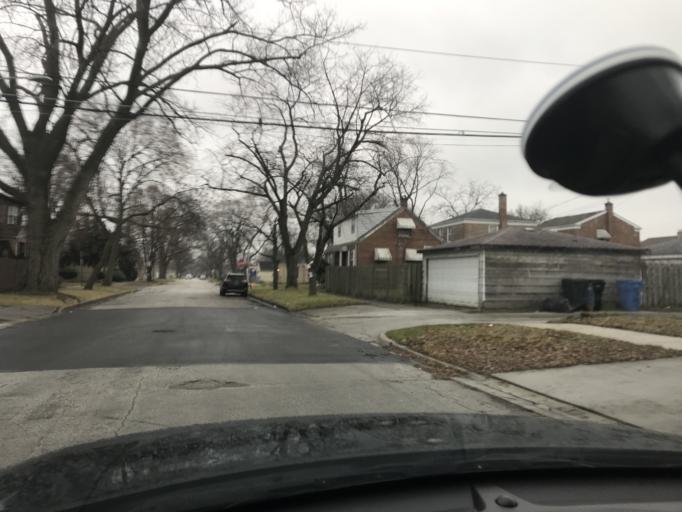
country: US
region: Illinois
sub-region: Cook County
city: Evergreen Park
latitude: 41.7270
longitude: -87.6406
